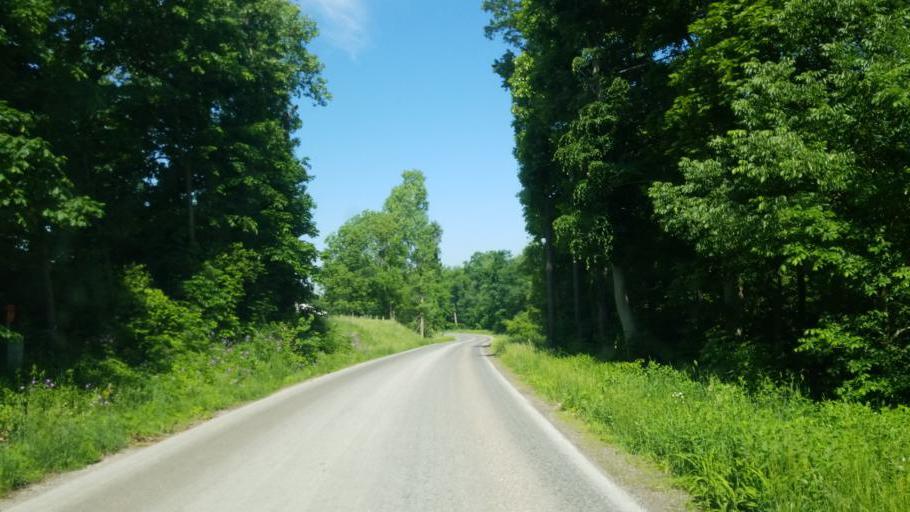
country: US
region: Ohio
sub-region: Tuscarawas County
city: Sugarcreek
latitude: 40.4460
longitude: -81.7775
